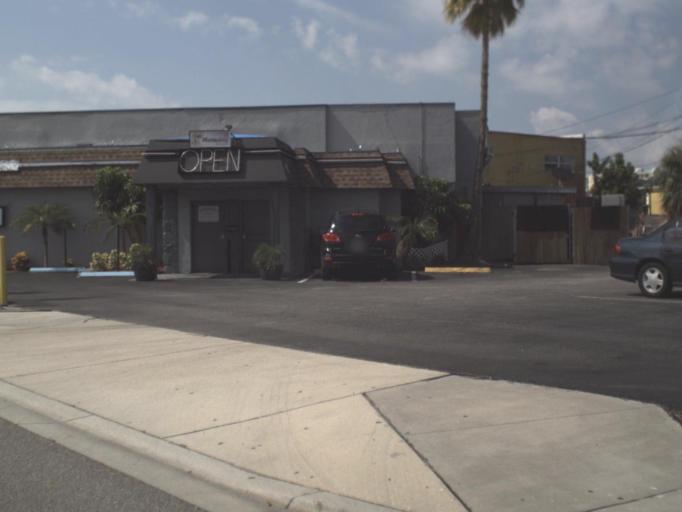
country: US
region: Florida
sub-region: Pinellas County
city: South Pasadena
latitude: 27.7433
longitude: -82.7509
